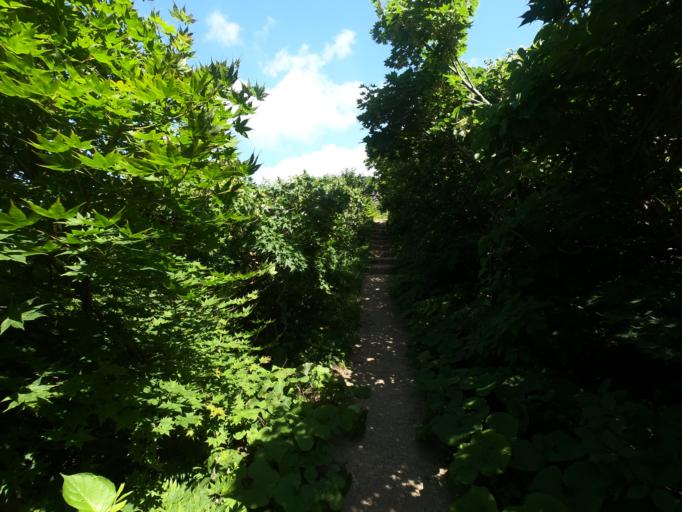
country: JP
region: Akita
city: Yuzawa
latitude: 38.9783
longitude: 140.7723
